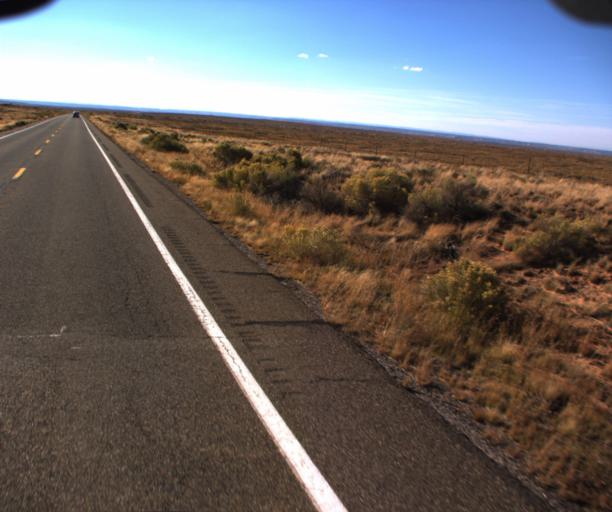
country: US
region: Arizona
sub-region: Coconino County
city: Kaibito
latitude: 36.6142
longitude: -110.9984
